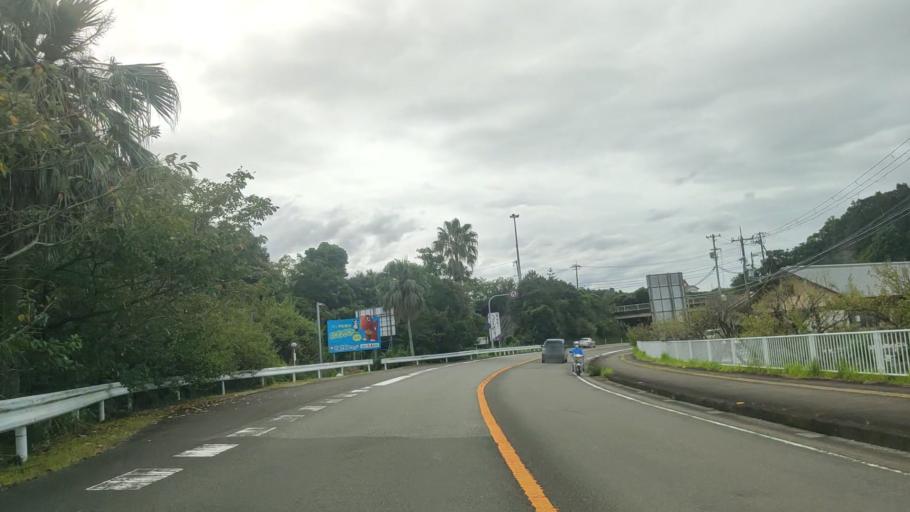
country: JP
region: Wakayama
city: Tanabe
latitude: 33.6950
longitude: 135.3885
